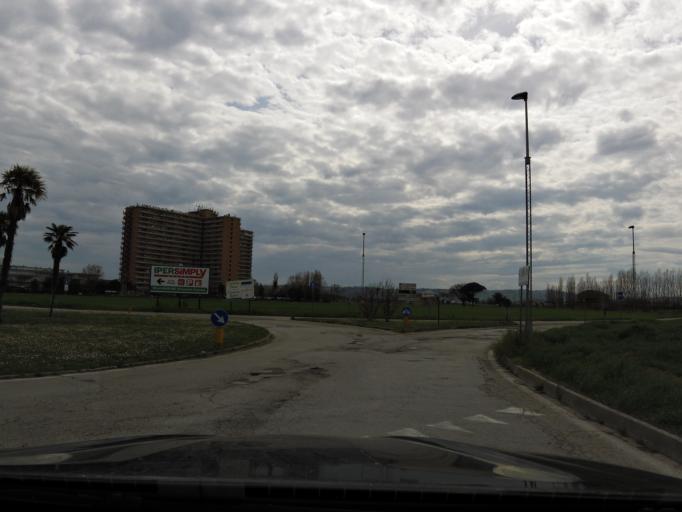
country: IT
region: The Marches
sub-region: Provincia di Macerata
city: Porto Recanati
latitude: 43.4201
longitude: 13.6647
